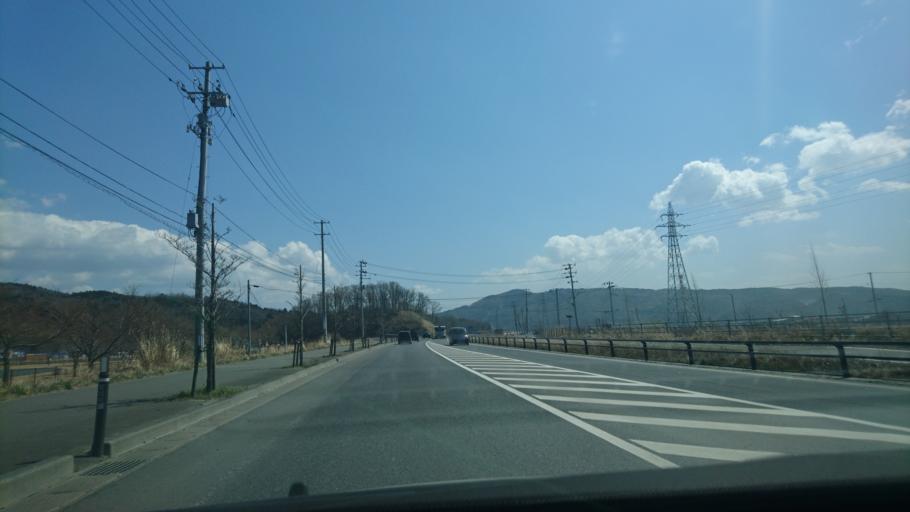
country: JP
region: Miyagi
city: Ishinomaki
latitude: 38.4546
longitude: 141.3077
